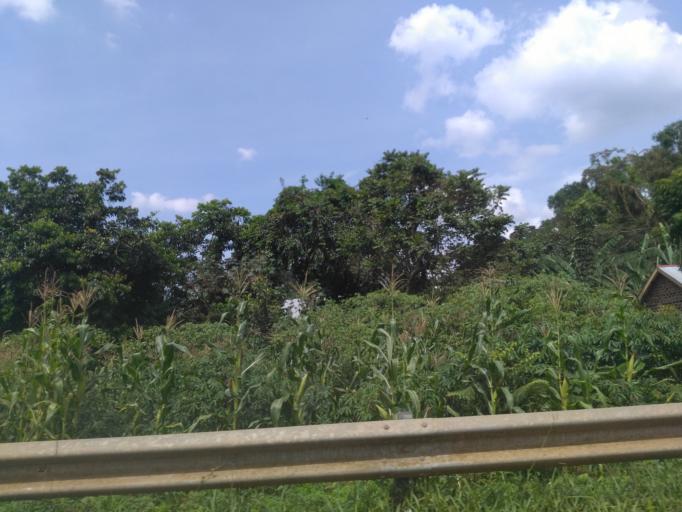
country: UG
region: Central Region
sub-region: Wakiso District
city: Bweyogerere
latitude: 0.4852
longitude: 32.6097
